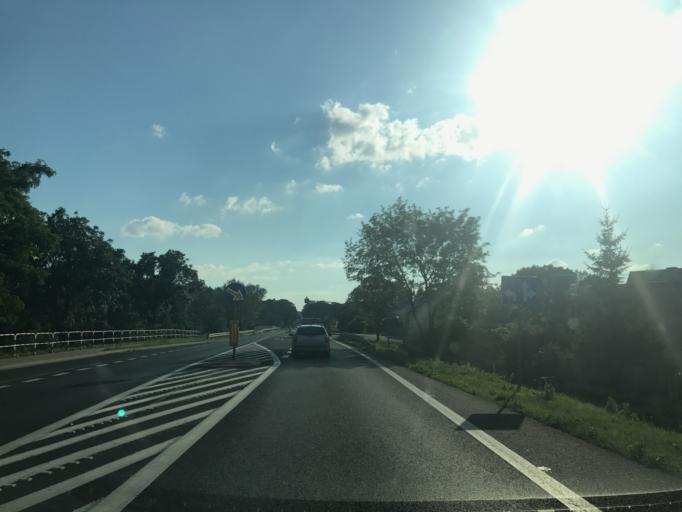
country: PL
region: Greater Poland Voivodeship
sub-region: Powiat kolski
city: Koscielec
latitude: 52.1772
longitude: 18.5837
